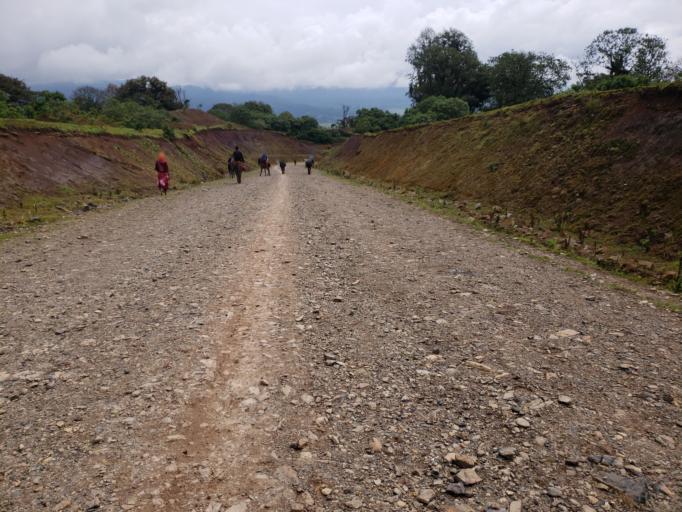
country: ET
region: Oromiya
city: Dodola
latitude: 6.6489
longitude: 39.3684
